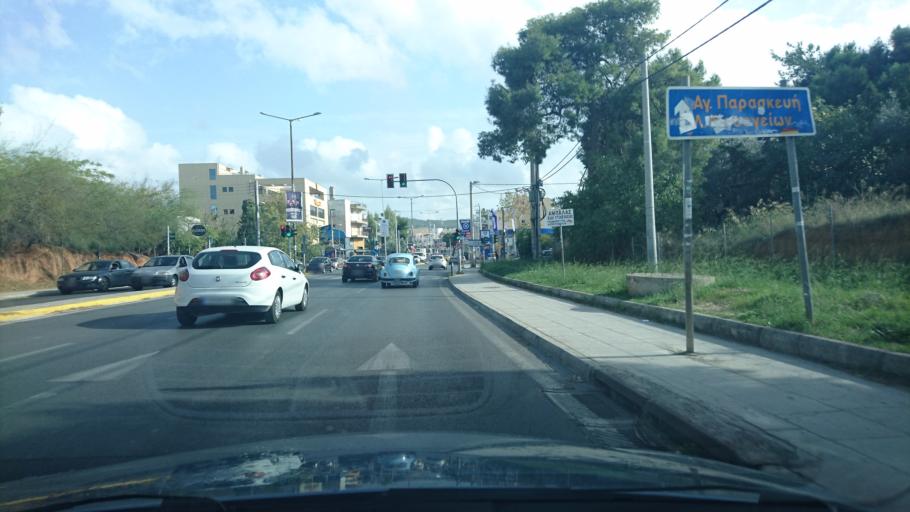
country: GR
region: Attica
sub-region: Nomarchia Athinas
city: Khalandrion
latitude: 38.0159
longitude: 23.8148
